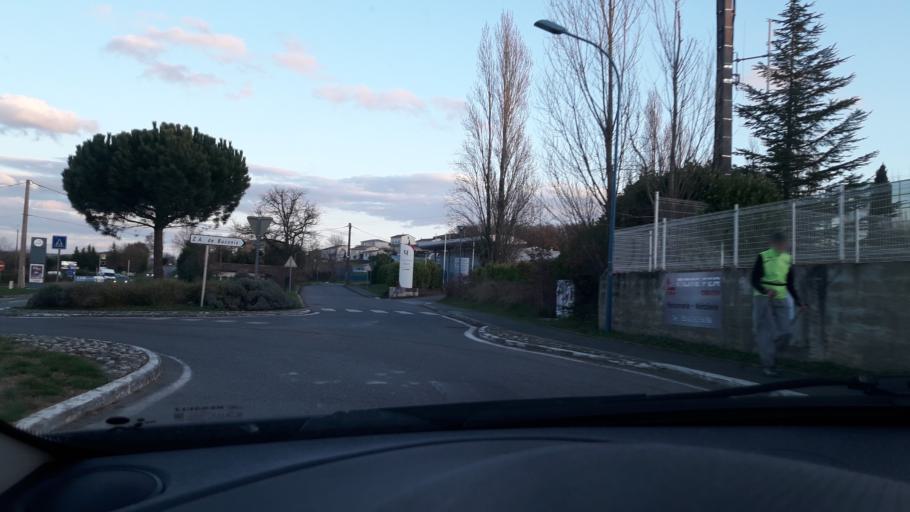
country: FR
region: Midi-Pyrenees
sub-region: Departement du Gers
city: Pujaudran
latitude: 43.6044
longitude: 1.1013
